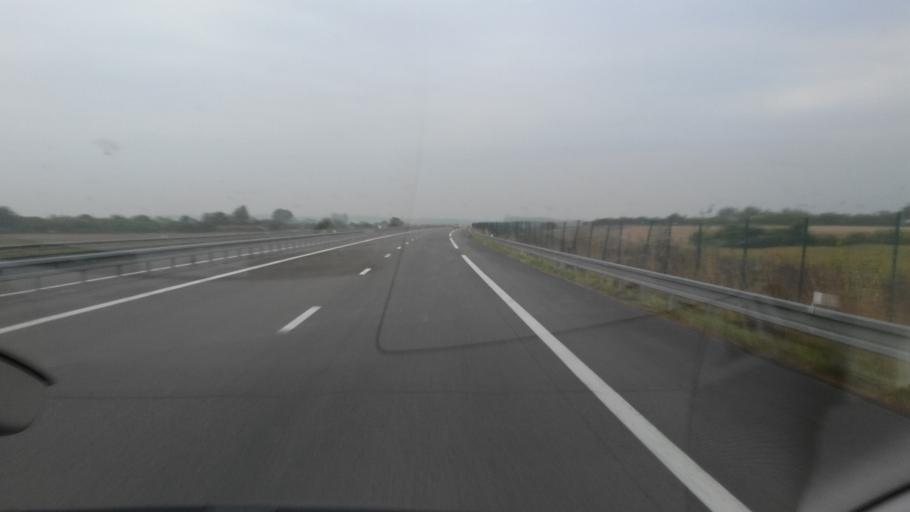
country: FR
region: Champagne-Ardenne
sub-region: Departement des Ardennes
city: Rethel
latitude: 49.5538
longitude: 4.4534
